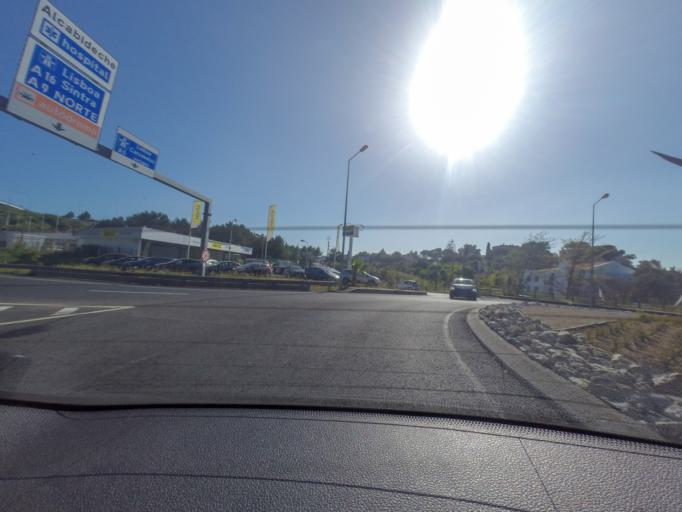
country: PT
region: Lisbon
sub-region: Cascais
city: Alcabideche
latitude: 38.7241
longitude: -9.4173
